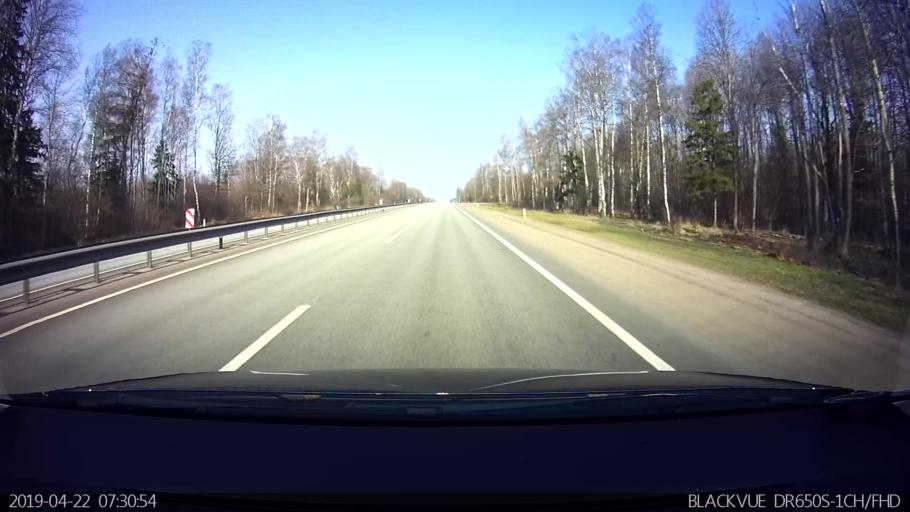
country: RU
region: Smolensk
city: Vyaz'ma
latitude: 55.1952
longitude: 33.9324
